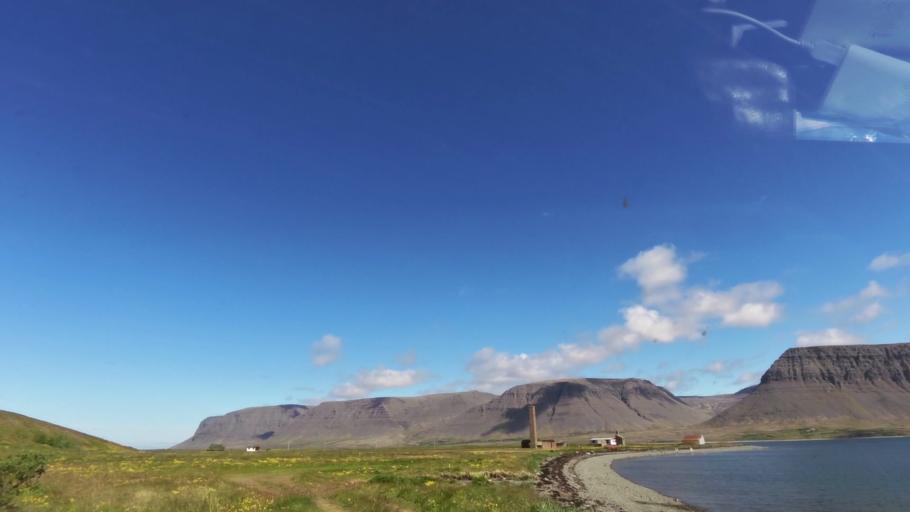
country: IS
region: West
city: Olafsvik
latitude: 65.6372
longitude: -23.9323
